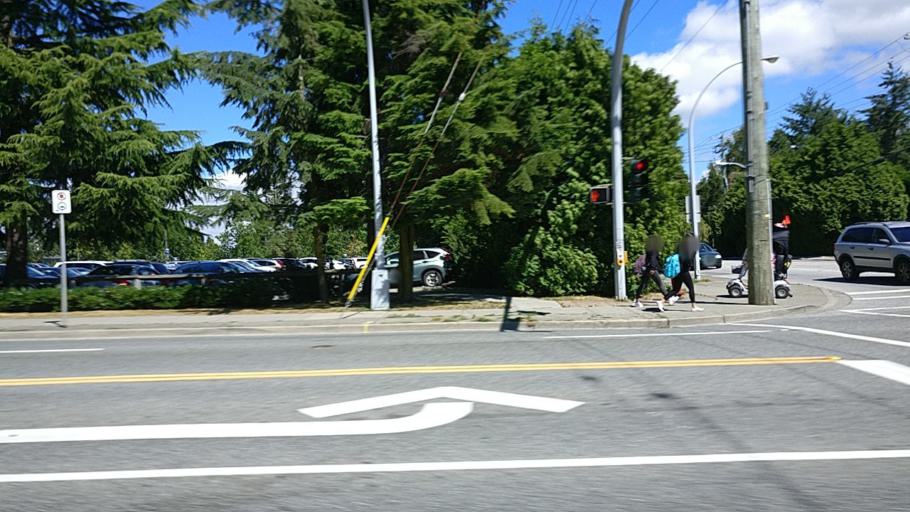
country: CA
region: British Columbia
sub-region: Greater Vancouver Regional District
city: White Rock
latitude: 49.0310
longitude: -122.7904
